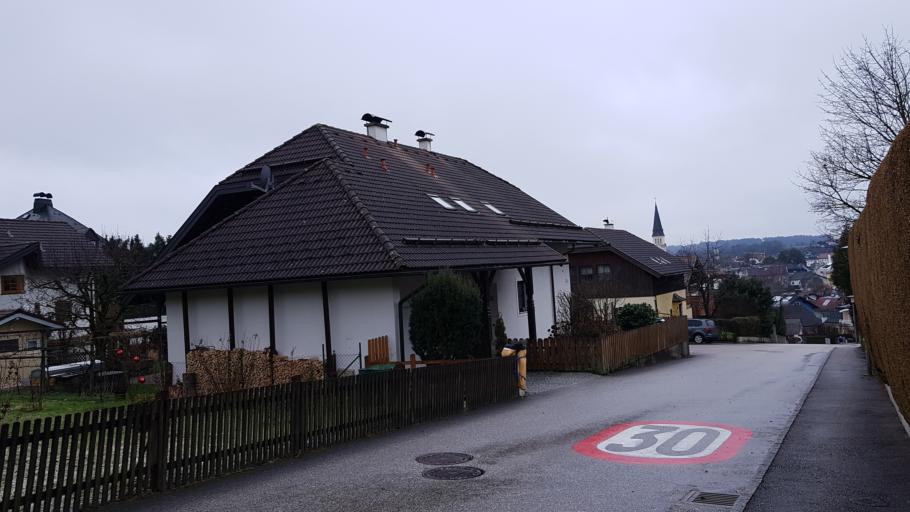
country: AT
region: Salzburg
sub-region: Politischer Bezirk Salzburg-Umgebung
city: Oberndorf bei Salzburg
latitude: 47.9401
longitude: 12.9491
